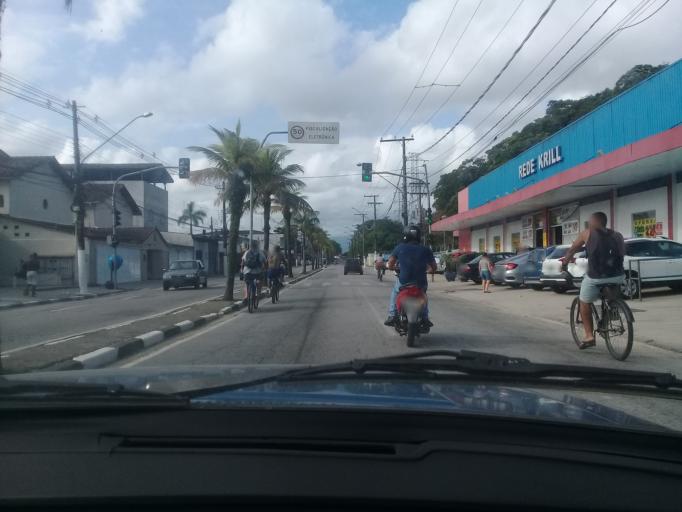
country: BR
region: Sao Paulo
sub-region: Guaruja
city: Guaruja
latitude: -24.0002
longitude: -46.2740
